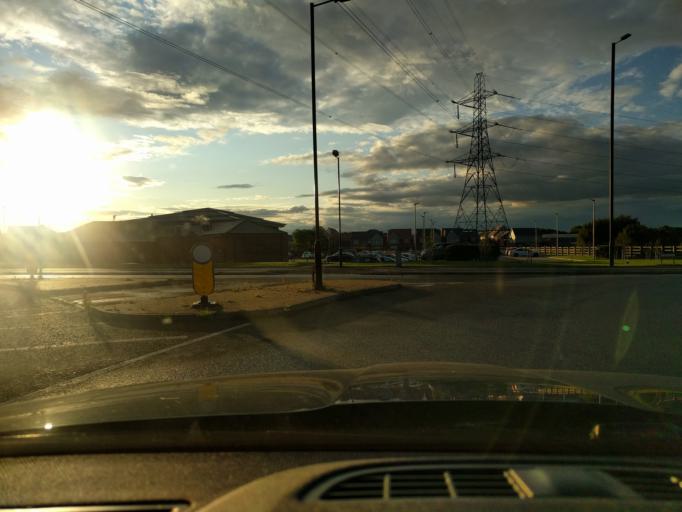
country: GB
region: England
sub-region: Northumberland
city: Backworth
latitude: 55.0341
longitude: -1.5234
